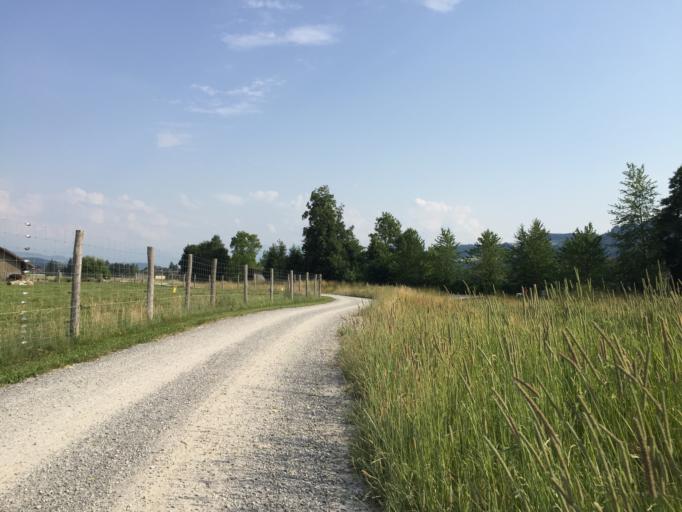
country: CH
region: Bern
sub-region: Bern-Mittelland District
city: Rubigen
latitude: 46.8896
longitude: 7.5467
